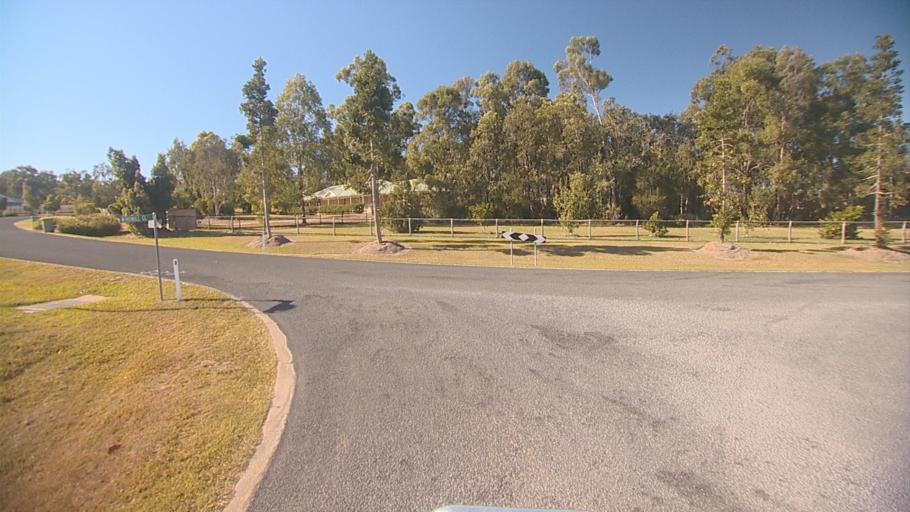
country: AU
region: Queensland
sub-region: Logan
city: North Maclean
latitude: -27.7360
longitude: 152.9555
